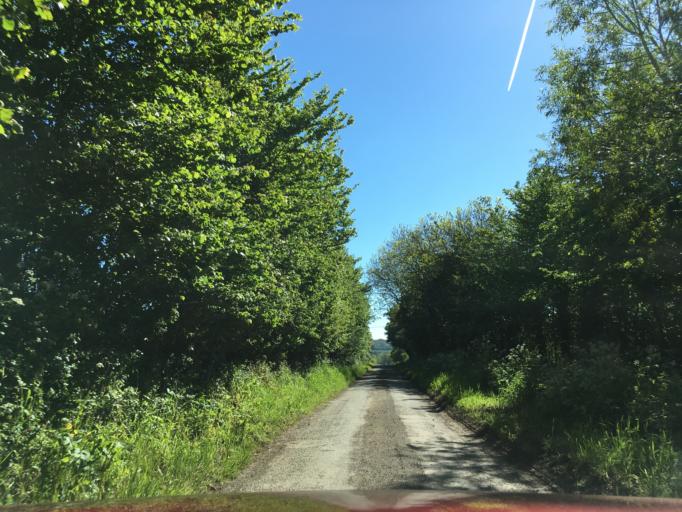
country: GB
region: England
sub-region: South Gloucestershire
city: Almondsbury
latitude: 51.5886
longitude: -2.6027
